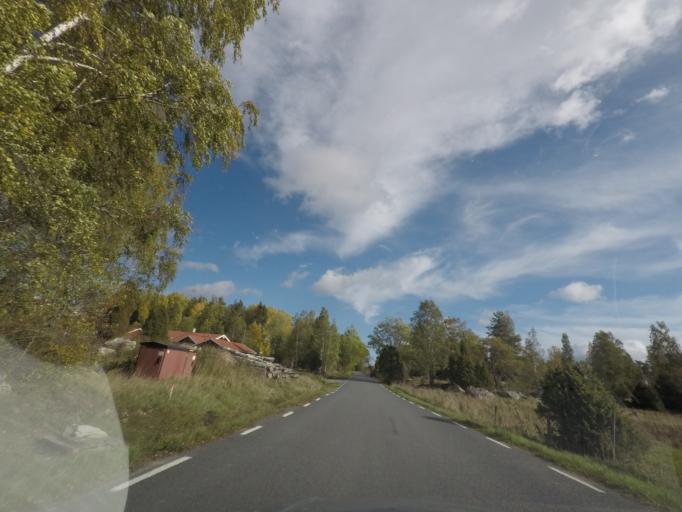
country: SE
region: Soedermanland
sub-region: Eskilstuna Kommun
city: Kvicksund
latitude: 59.3147
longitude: 16.2583
